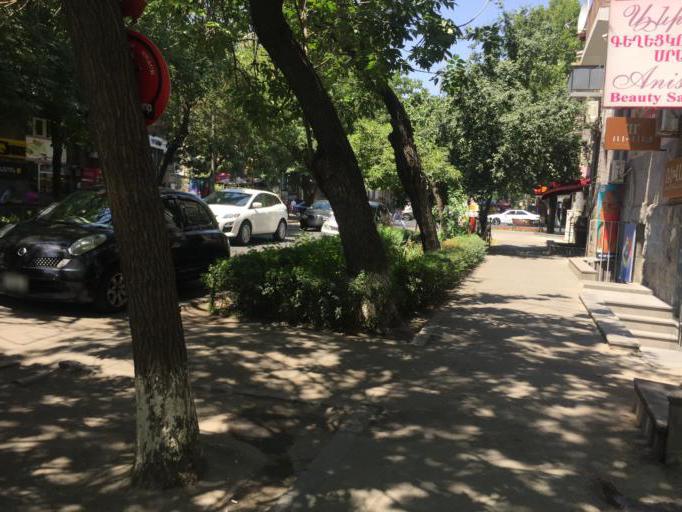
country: AM
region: Yerevan
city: Yerevan
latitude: 40.1833
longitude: 44.5118
